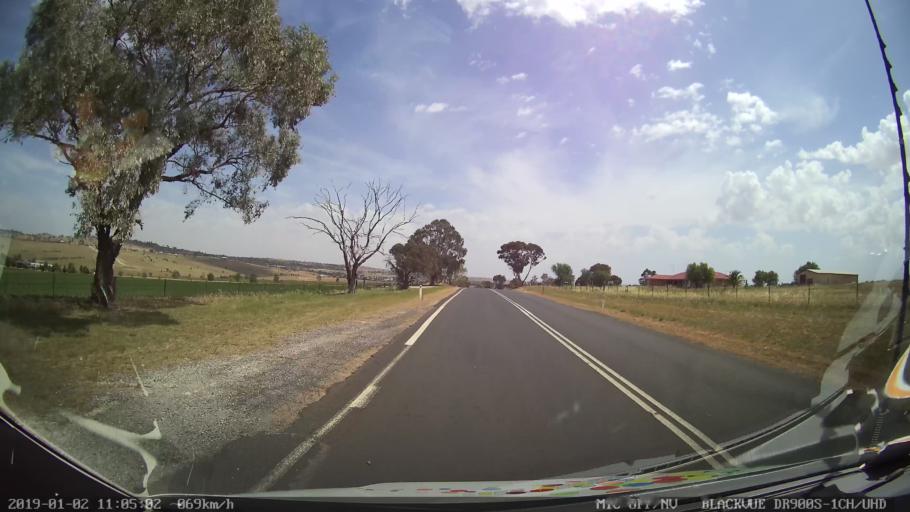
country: AU
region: New South Wales
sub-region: Young
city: Young
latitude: -34.5695
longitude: 148.3541
